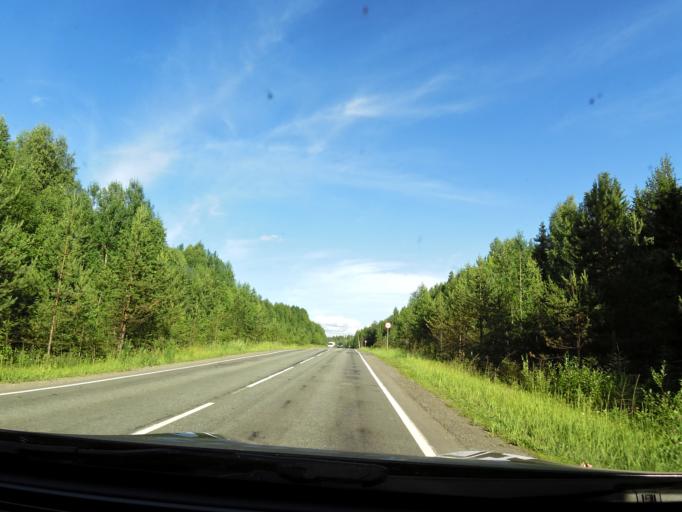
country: RU
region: Kirov
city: Chernaya Kholunitsa
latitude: 58.8663
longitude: 51.5716
